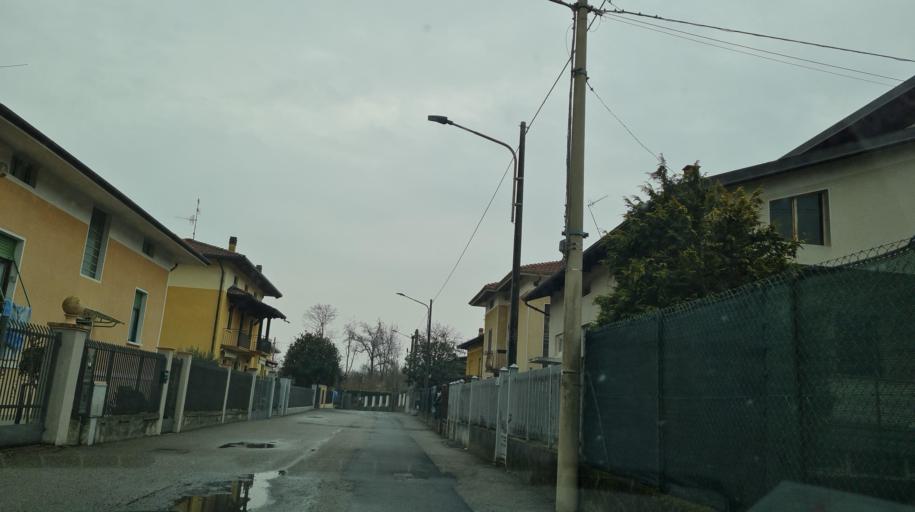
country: IT
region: Piedmont
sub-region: Provincia di Biella
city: Ceresane-Curanuova
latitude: 45.5127
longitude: 8.0051
